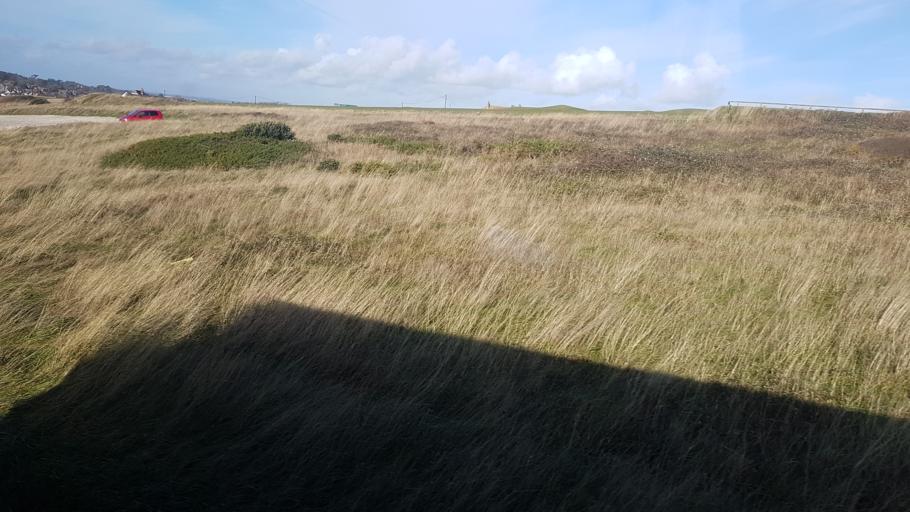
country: GB
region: England
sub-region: Isle of Wight
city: Freshwater
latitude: 50.6692
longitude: -1.5030
